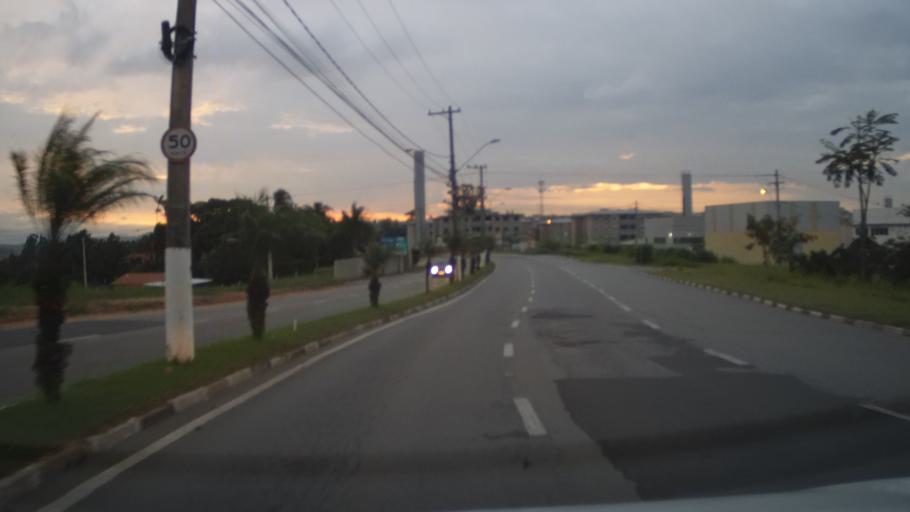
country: BR
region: Sao Paulo
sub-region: Vinhedo
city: Vinhedo
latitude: -23.0380
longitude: -46.9986
